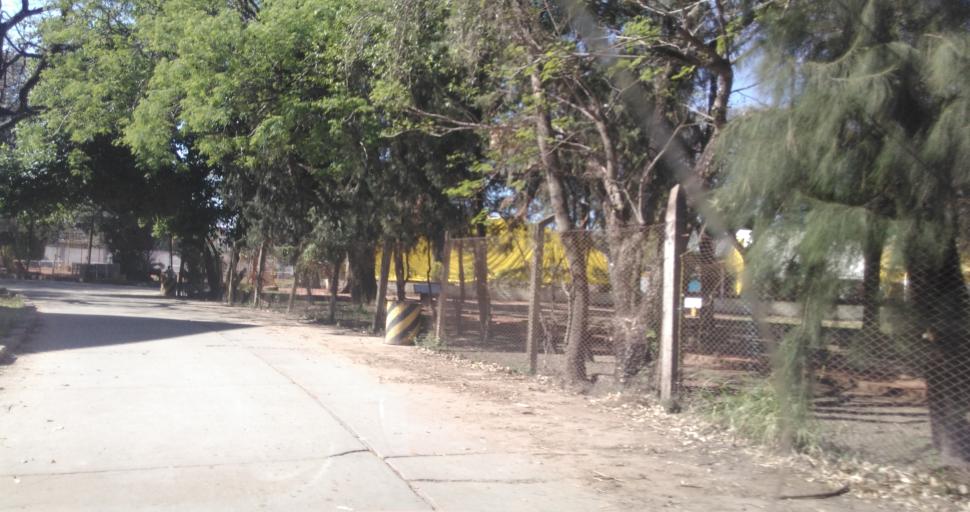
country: AR
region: Chaco
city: Resistencia
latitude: -27.4653
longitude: -58.9825
